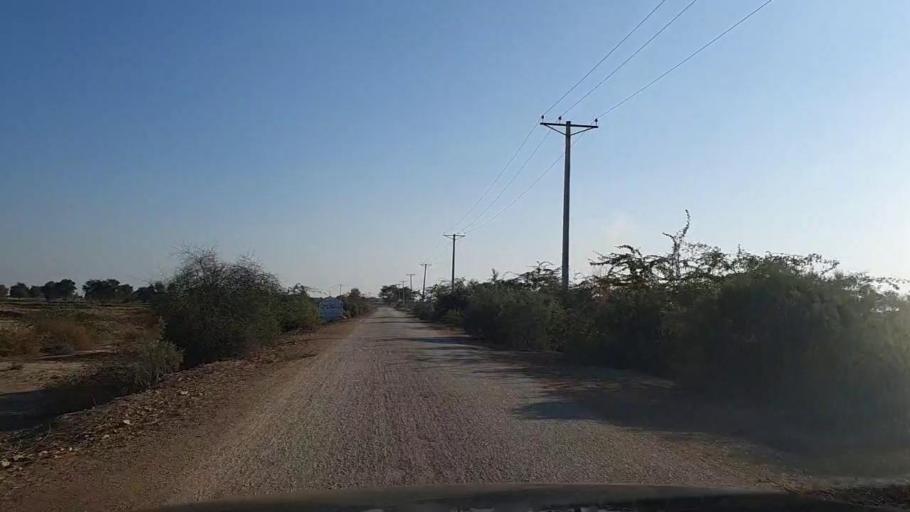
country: PK
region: Sindh
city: Nawabshah
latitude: 26.2115
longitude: 68.3737
